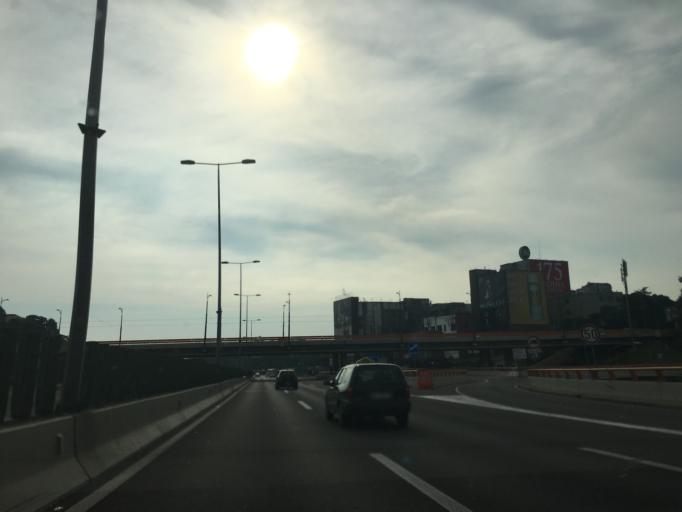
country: RS
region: Central Serbia
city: Belgrade
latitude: 44.7984
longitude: 20.4490
